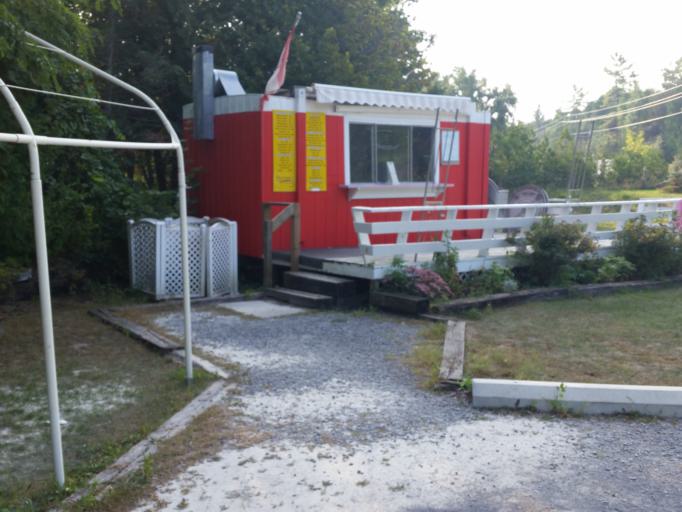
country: CA
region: Ontario
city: Prince Edward
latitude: 43.9015
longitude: -77.2272
